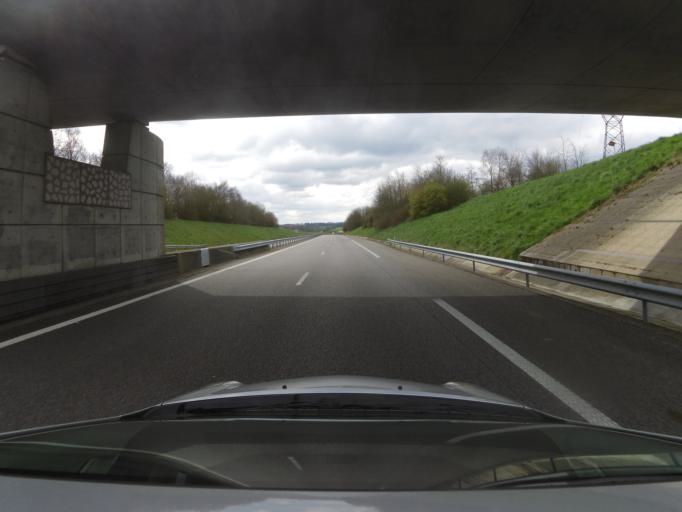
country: FR
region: Haute-Normandie
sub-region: Departement de la Seine-Maritime
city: Beuzeville-la-Grenier
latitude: 49.5760
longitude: 0.4111
